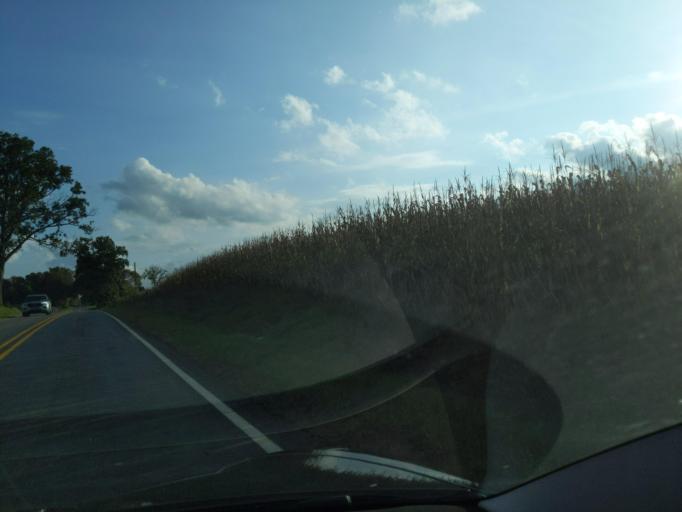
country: US
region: Michigan
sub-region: Ingham County
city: Leslie
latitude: 42.3709
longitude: -84.4629
